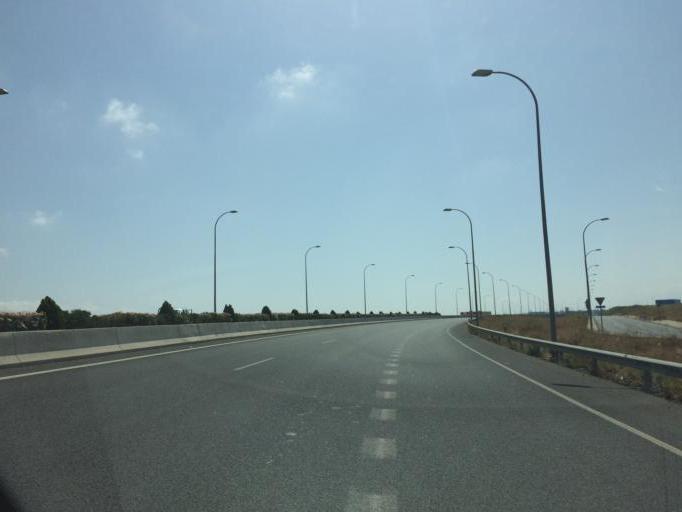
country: ES
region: Andalusia
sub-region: Provincia de Malaga
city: Alhaurin de la Torre
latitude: 36.6890
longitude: -4.5112
